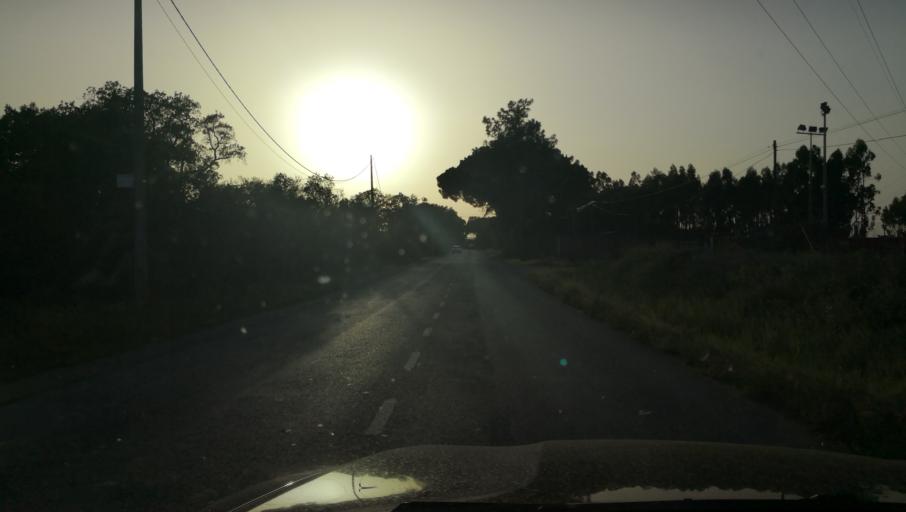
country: PT
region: Setubal
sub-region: Setubal
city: Setubal
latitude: 38.5388
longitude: -8.8311
